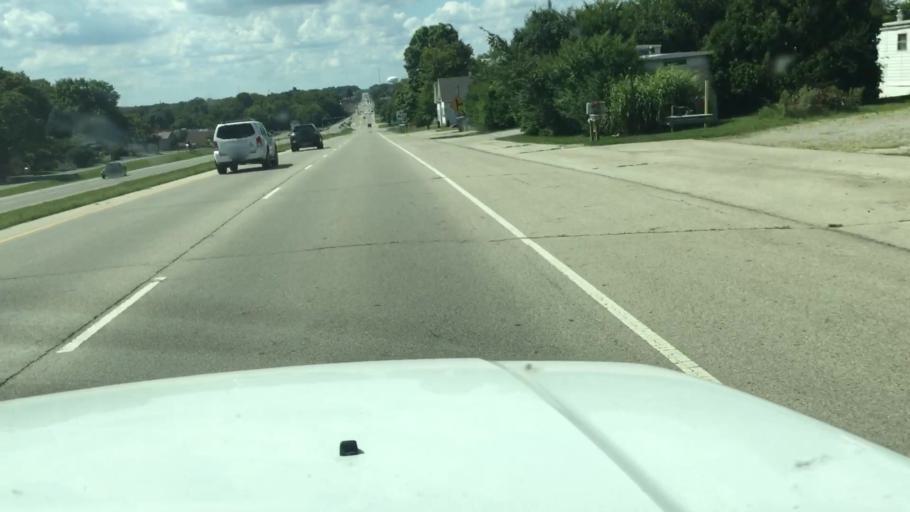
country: US
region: Ohio
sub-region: Clark County
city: Springfield
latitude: 39.9234
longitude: -83.7527
